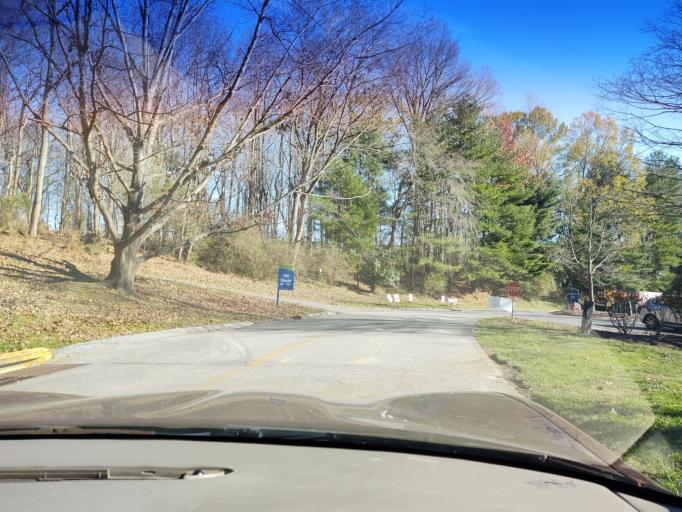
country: US
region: Maryland
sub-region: Baltimore County
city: Hunt Valley
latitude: 39.5037
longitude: -76.6429
